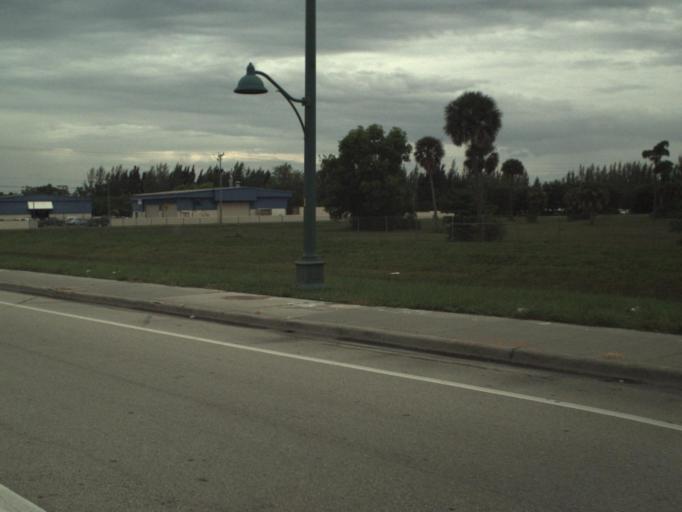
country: US
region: Florida
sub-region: Palm Beach County
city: Royal Palm Beach
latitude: 26.6807
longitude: -80.2087
